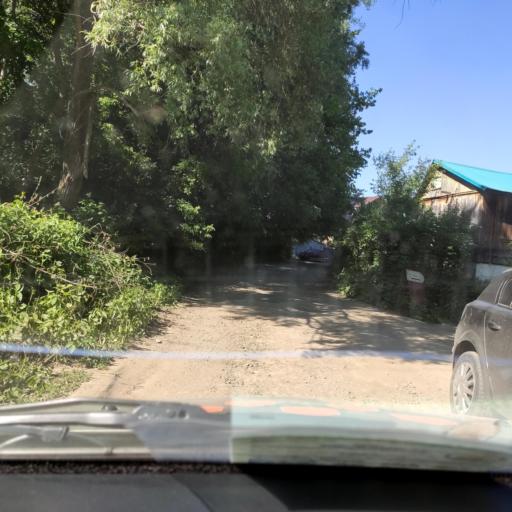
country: RU
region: Bashkortostan
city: Ufa
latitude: 54.7848
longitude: 56.1848
